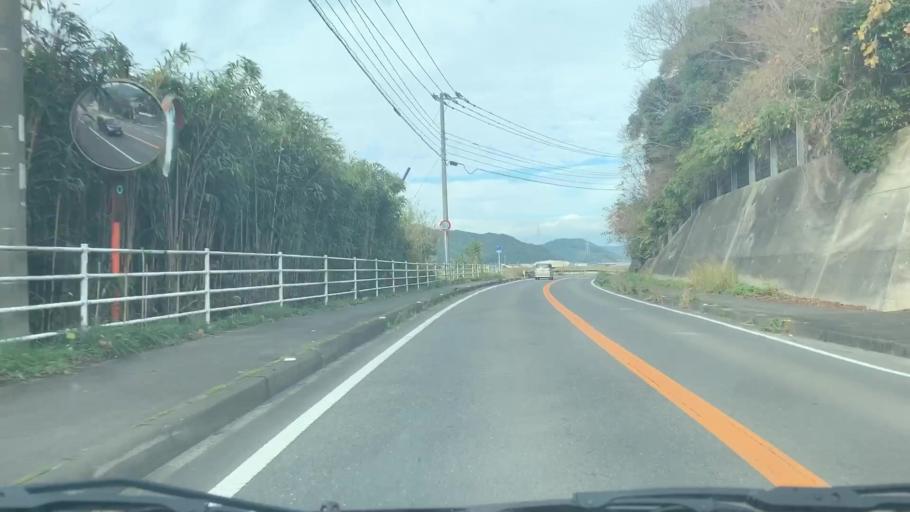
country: JP
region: Saga Prefecture
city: Karatsu
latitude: 33.3643
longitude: 130.0075
